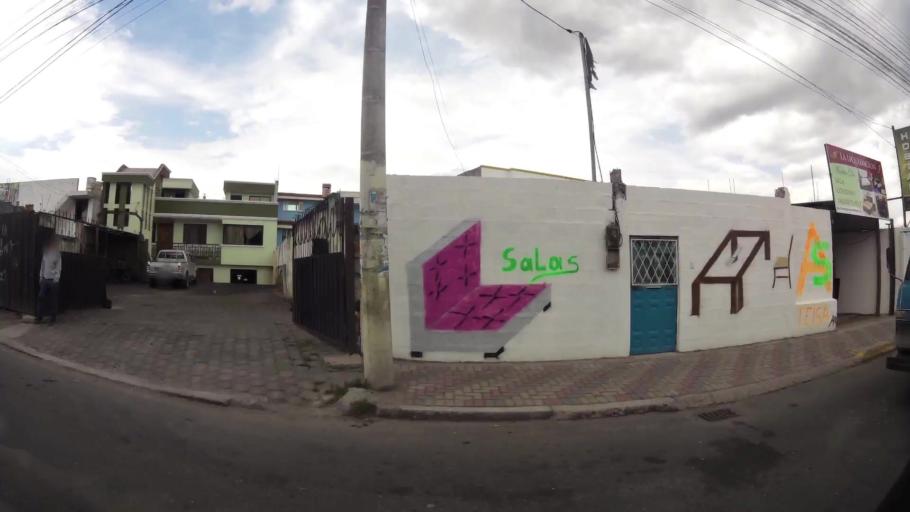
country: EC
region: Pichincha
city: Quito
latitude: -0.0914
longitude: -78.4322
